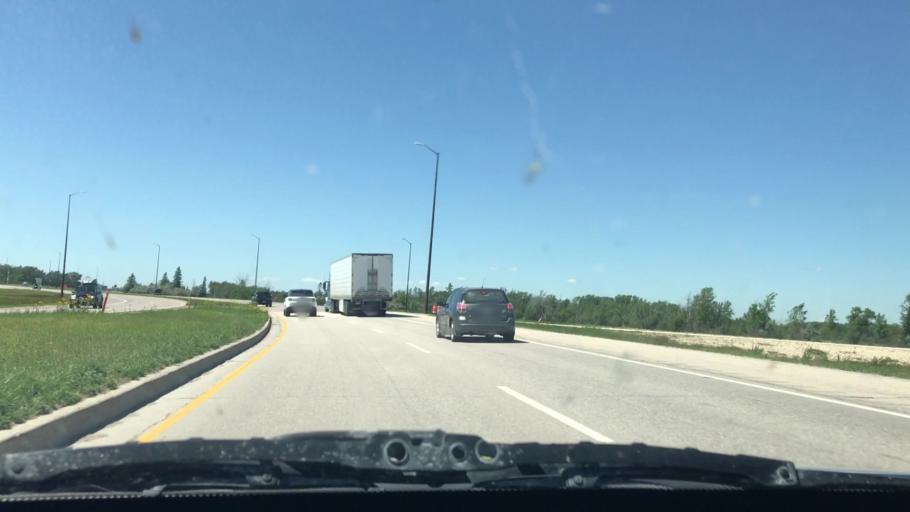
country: CA
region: Manitoba
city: Winnipeg
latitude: 49.8359
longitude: -96.9659
